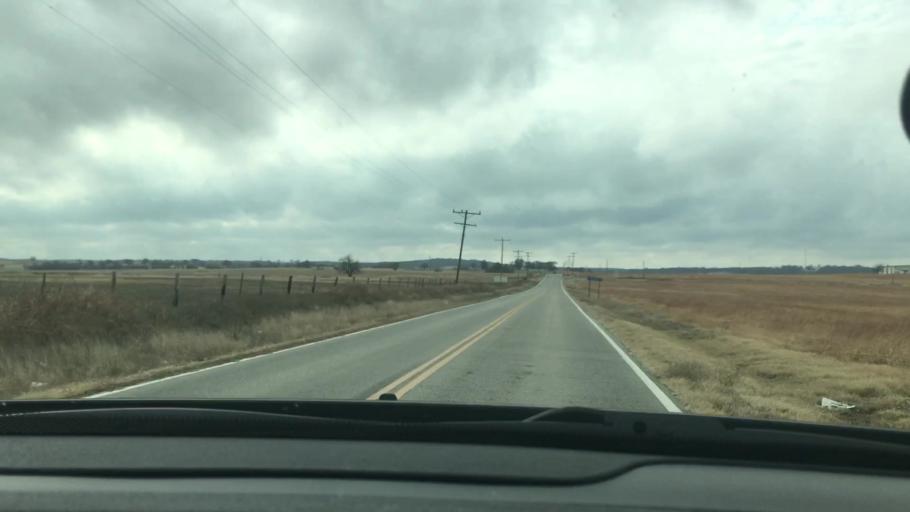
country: US
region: Oklahoma
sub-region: Bryan County
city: Durant
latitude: 34.1029
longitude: -96.4877
